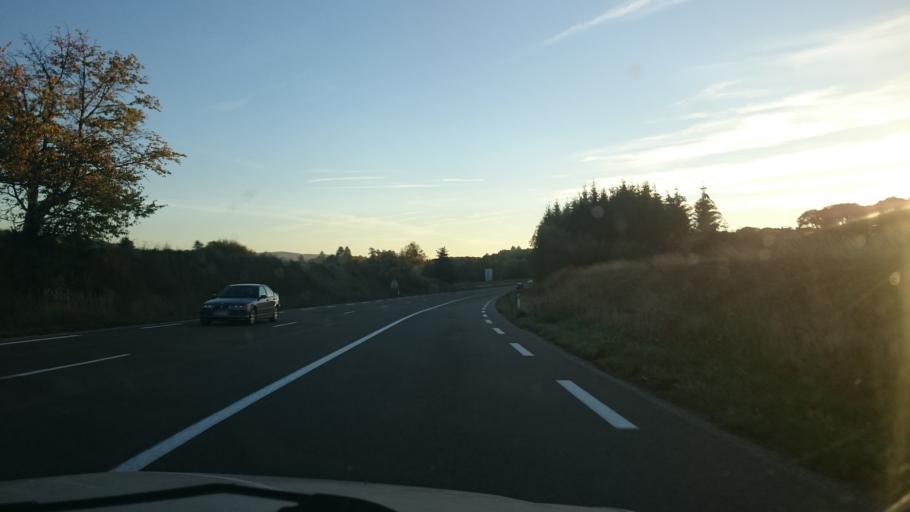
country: FR
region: Franche-Comte
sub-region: Departement du Jura
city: Mouchard
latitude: 46.9558
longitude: 5.7890
